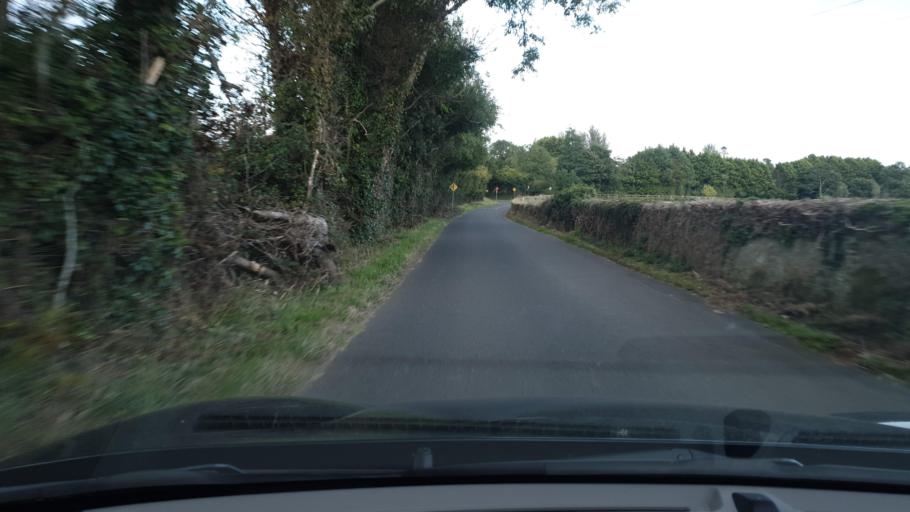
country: IE
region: Leinster
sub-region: South Dublin
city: Newcastle
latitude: 53.2656
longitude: -6.5161
